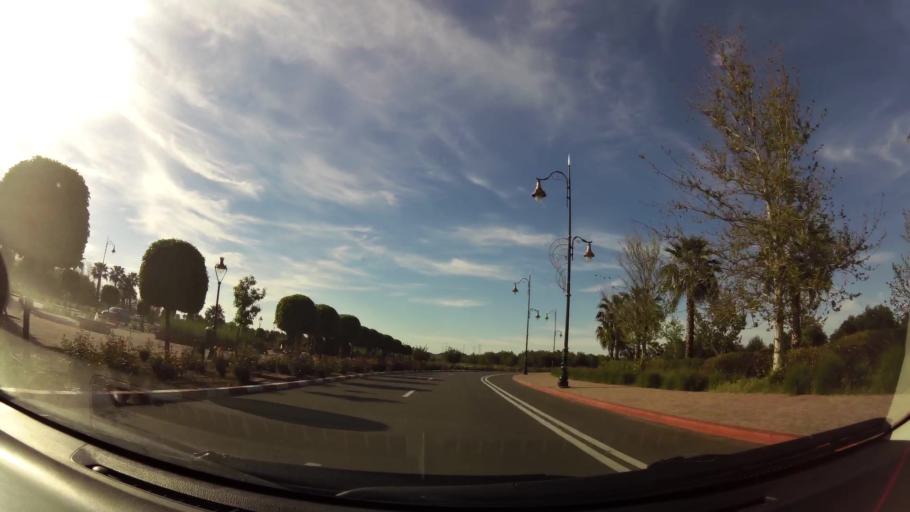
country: MA
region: Marrakech-Tensift-Al Haouz
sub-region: Marrakech
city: Marrakesh
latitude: 31.6119
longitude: -8.0041
